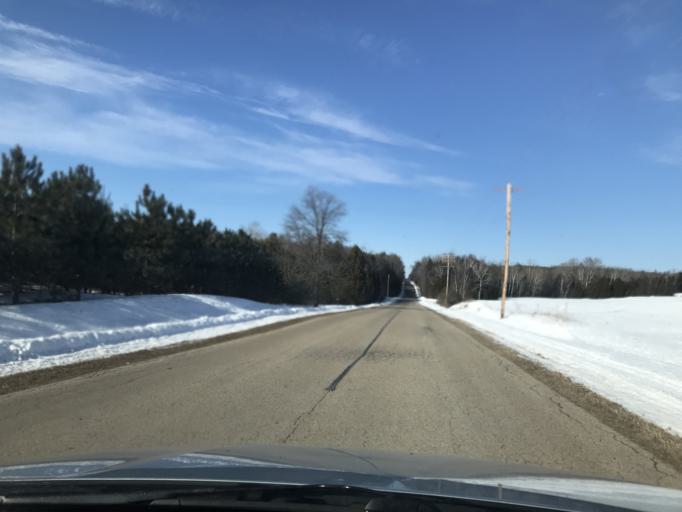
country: US
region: Wisconsin
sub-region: Oconto County
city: Gillett
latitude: 44.9615
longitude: -88.2723
